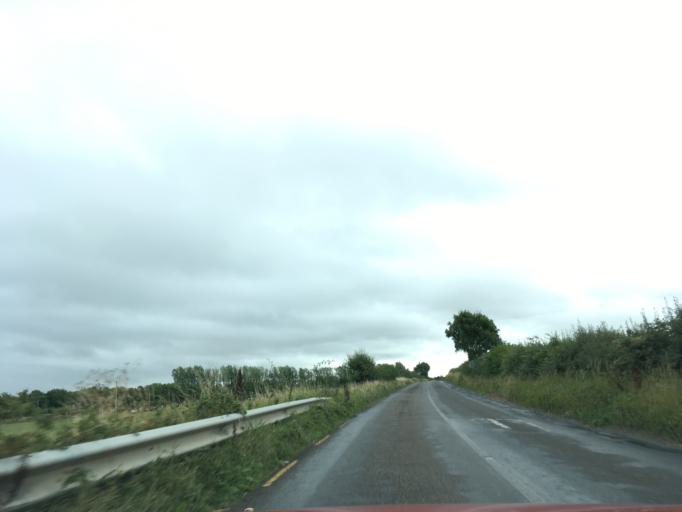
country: IE
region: Munster
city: Cashel
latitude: 52.4518
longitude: -7.8134
